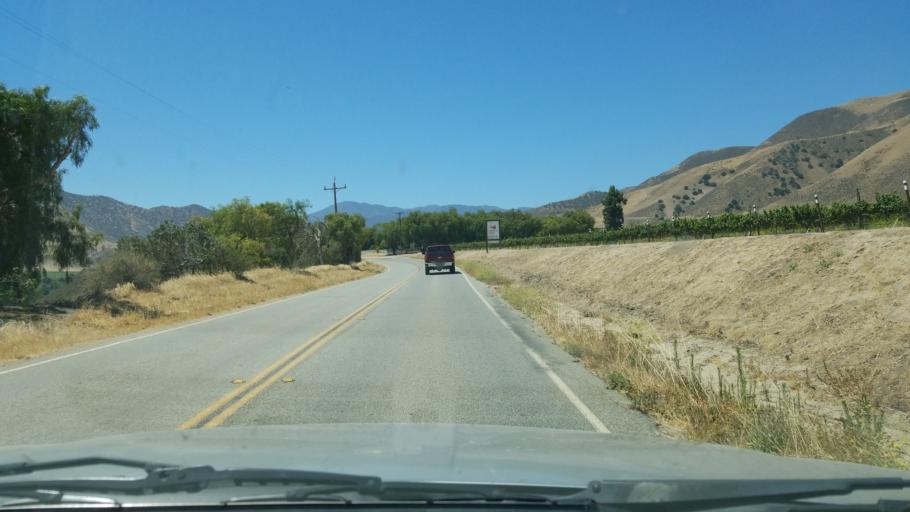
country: US
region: California
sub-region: Monterey County
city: Greenfield
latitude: 36.3033
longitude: -121.3122
